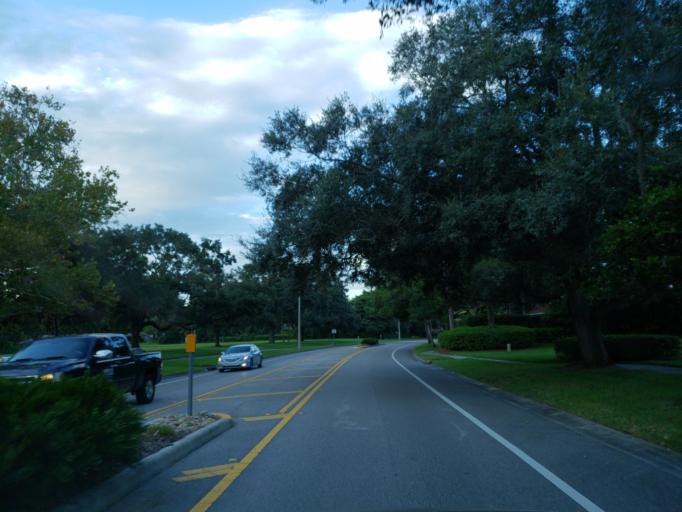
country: US
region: Florida
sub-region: Hillsborough County
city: Carrollwood Village
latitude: 28.0775
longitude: -82.5205
